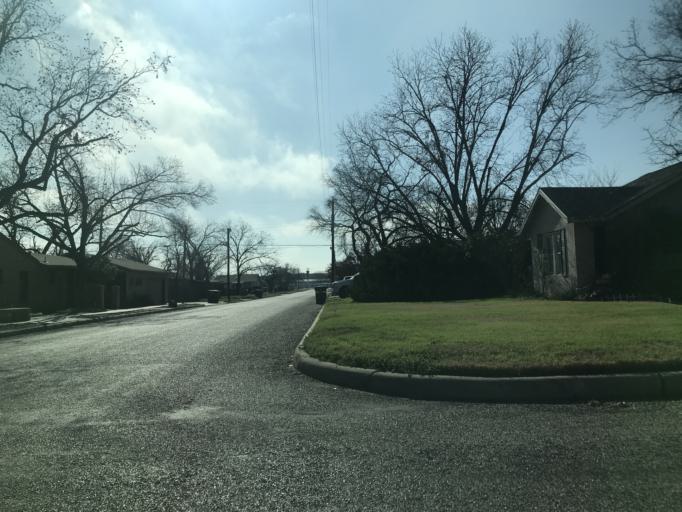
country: US
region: Texas
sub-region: Tom Green County
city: San Angelo
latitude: 31.4453
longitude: -100.4606
